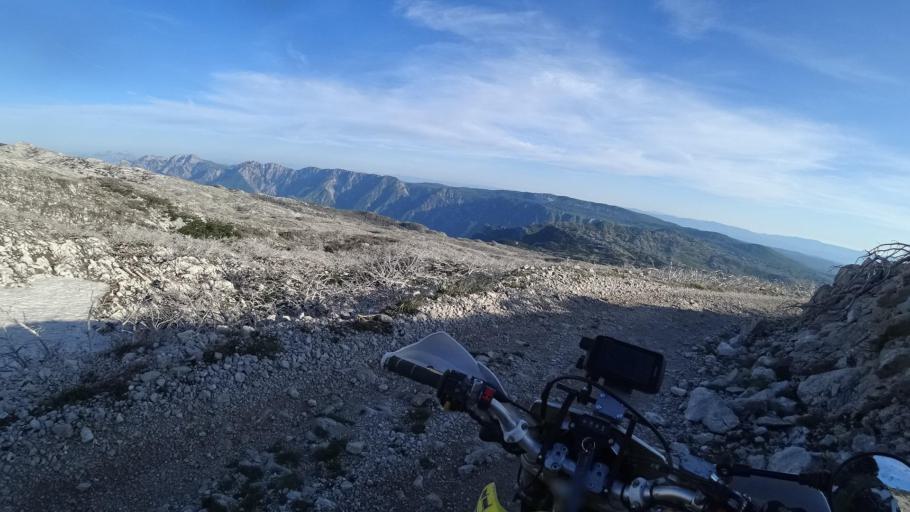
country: BA
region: Federation of Bosnia and Herzegovina
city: Kocerin
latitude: 43.5901
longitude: 17.5402
